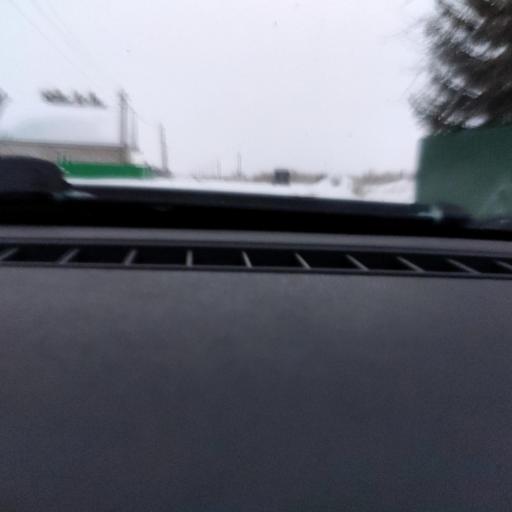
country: RU
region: Bashkortostan
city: Ulukulevo
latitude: 54.4037
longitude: 56.4490
